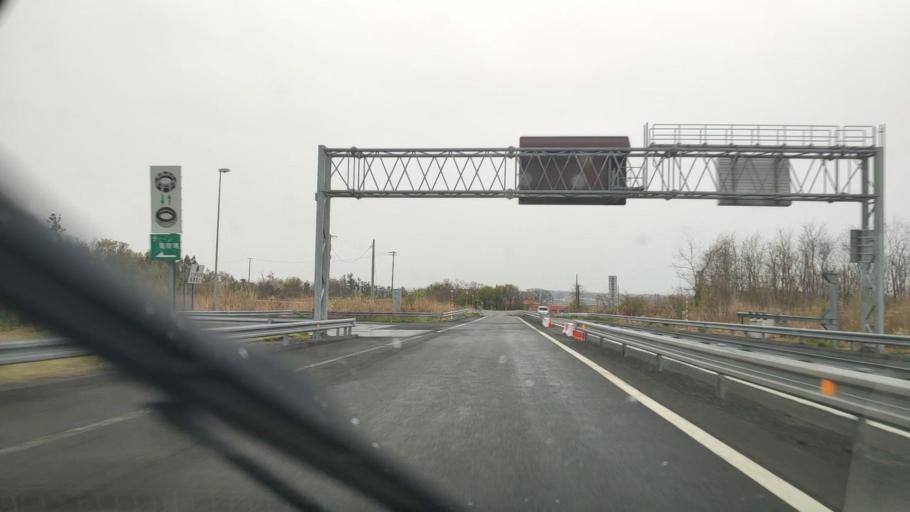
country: JP
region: Akita
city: Noshiromachi
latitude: 40.1176
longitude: 140.0095
